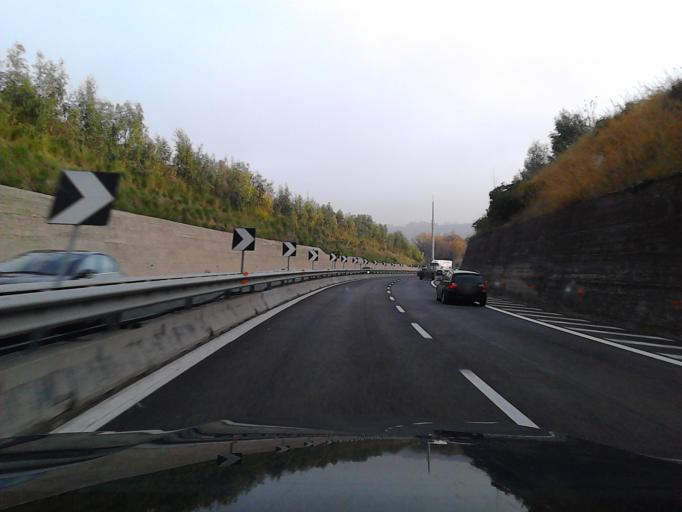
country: IT
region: Abruzzo
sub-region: Provincia di Chieti
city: San Vito Chietino
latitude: 42.2987
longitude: 14.4299
